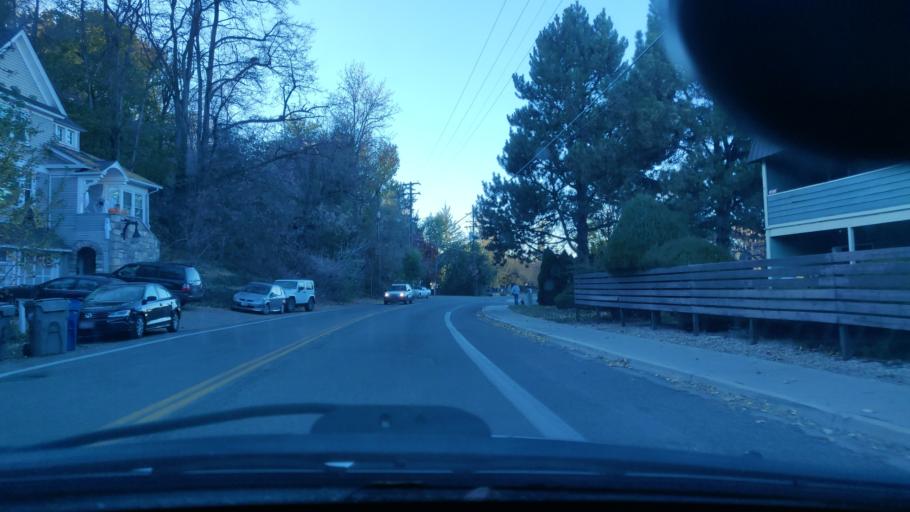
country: US
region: Idaho
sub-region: Ada County
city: Boise
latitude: 43.6018
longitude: -116.2104
